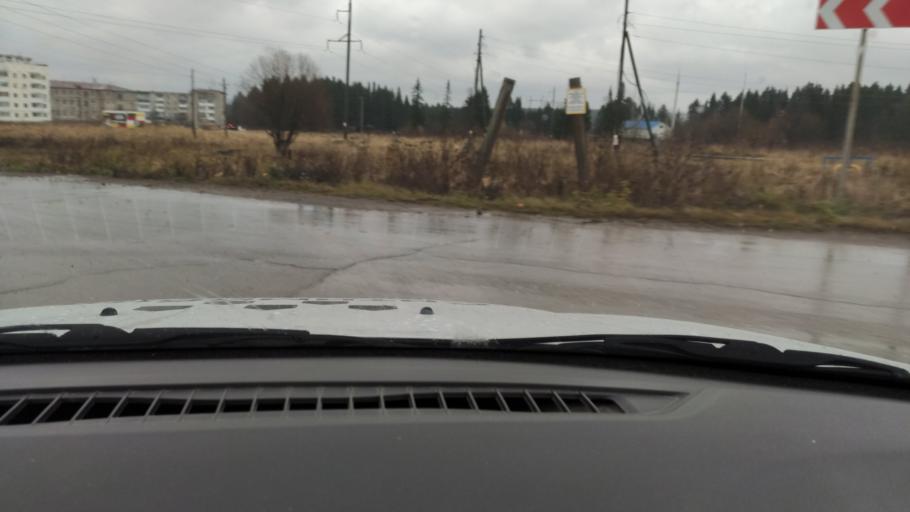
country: RU
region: Perm
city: Sylva
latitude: 58.0260
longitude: 56.7385
